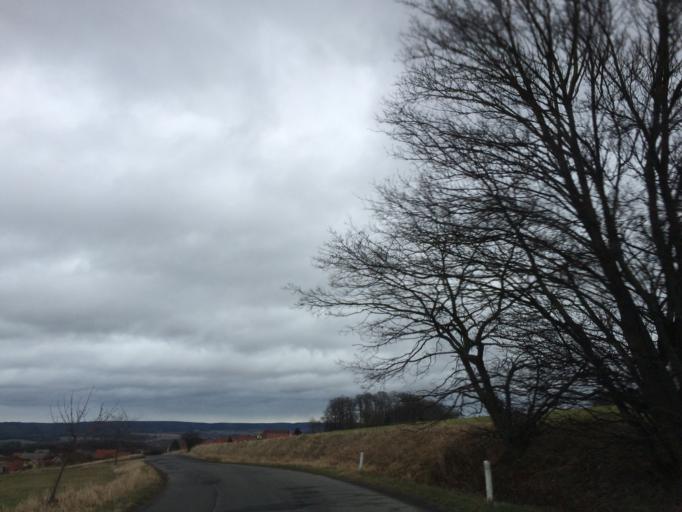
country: DE
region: Thuringia
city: Wernburg
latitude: 50.6737
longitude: 11.5940
